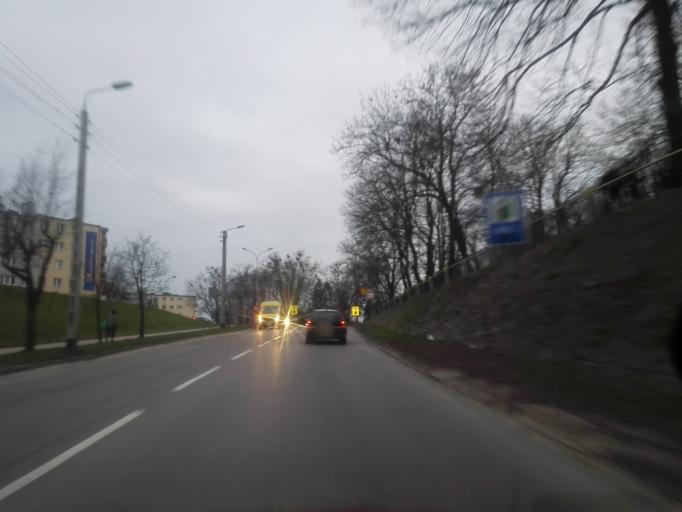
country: PL
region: Podlasie
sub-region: Lomza
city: Lomza
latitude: 53.1815
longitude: 22.0788
